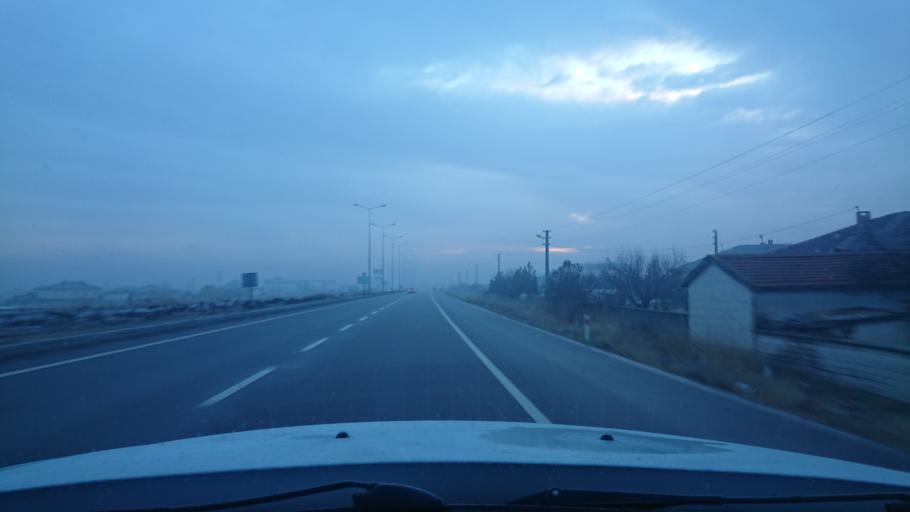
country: TR
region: Aksaray
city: Sultanhani
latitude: 38.2490
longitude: 33.5294
